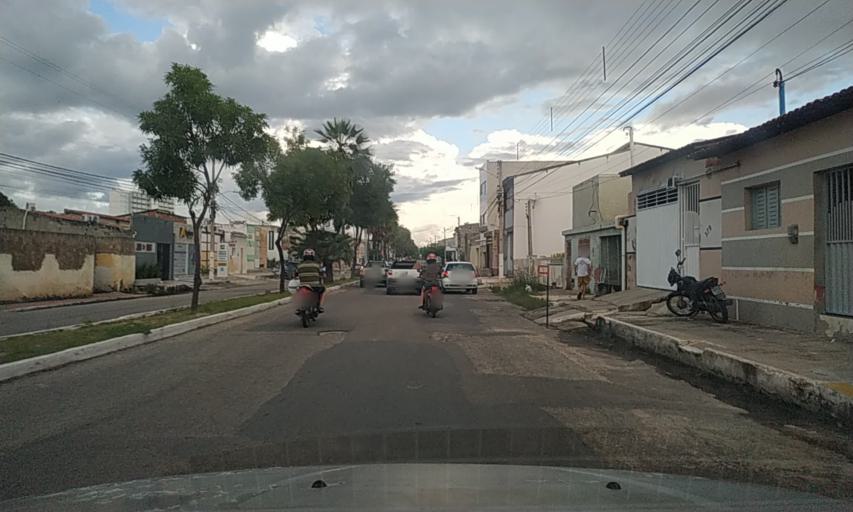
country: BR
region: Rio Grande do Norte
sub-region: Mossoro
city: Mossoro
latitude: -5.1867
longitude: -37.3529
